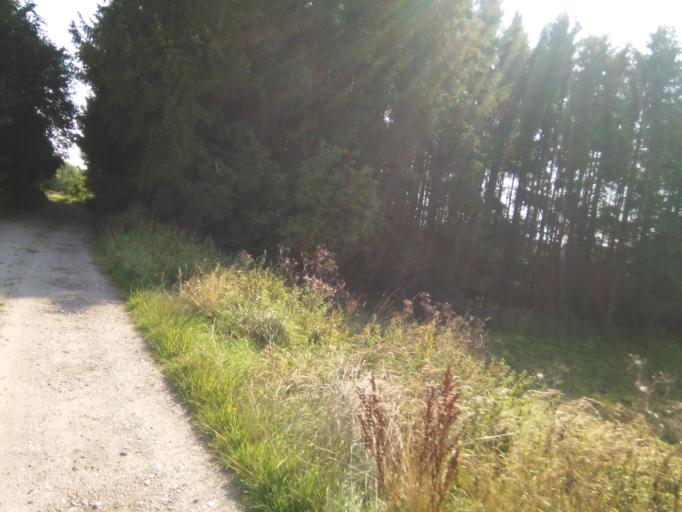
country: DK
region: Central Jutland
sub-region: Skanderborg Kommune
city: Skovby
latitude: 56.1339
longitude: 9.9847
